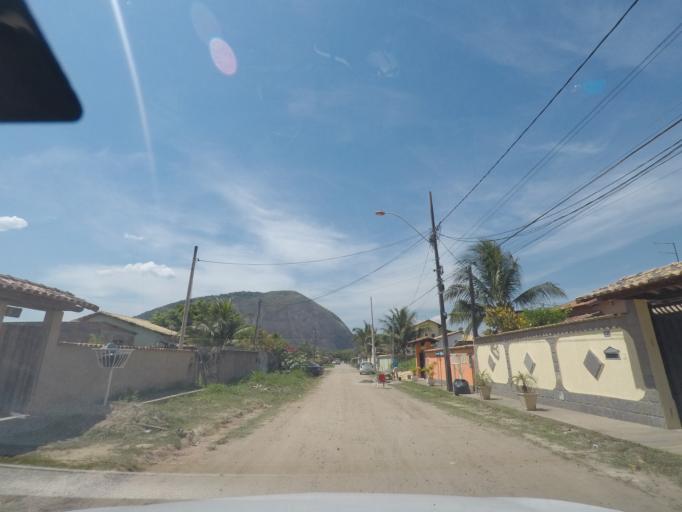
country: BR
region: Rio de Janeiro
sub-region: Marica
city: Marica
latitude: -22.9552
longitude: -42.9586
